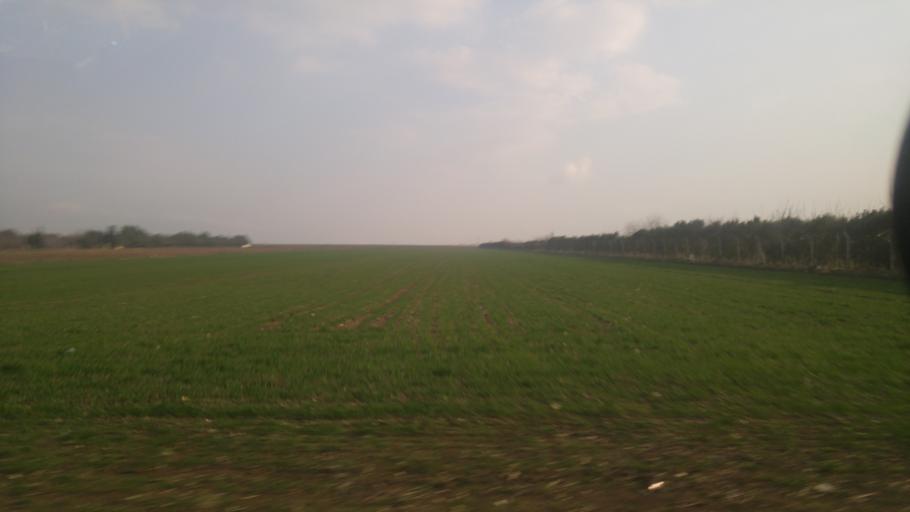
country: TR
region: Istanbul
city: Kavakli
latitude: 41.1120
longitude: 28.3003
